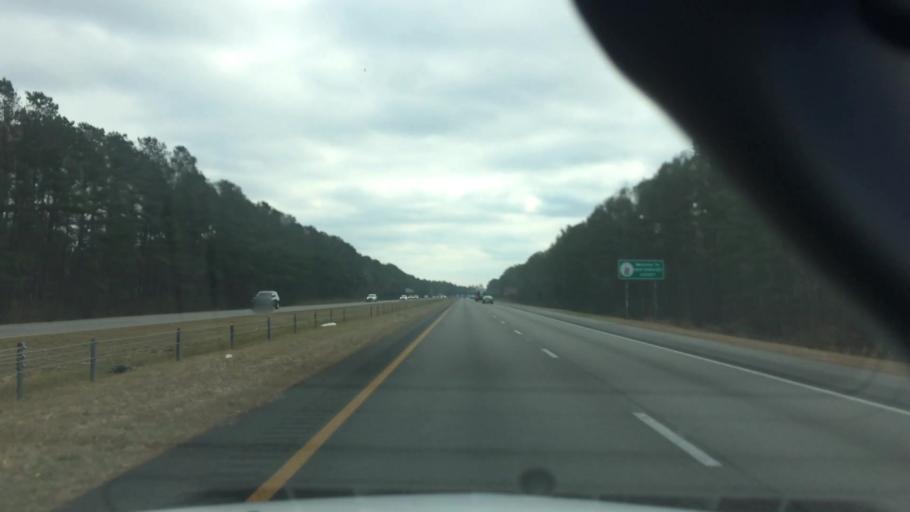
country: US
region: North Carolina
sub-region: New Hanover County
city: Skippers Corner
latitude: 34.3377
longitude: -77.8779
